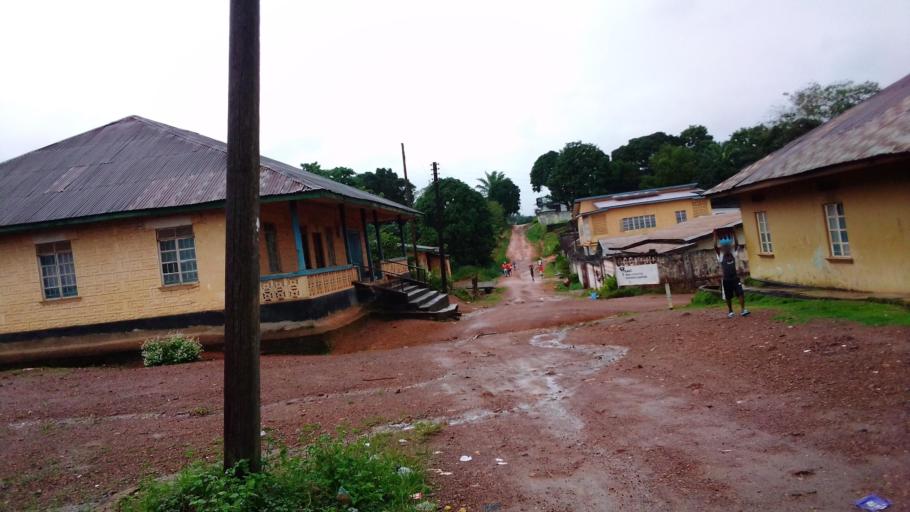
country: SL
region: Eastern Province
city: Kenema
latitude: 7.8903
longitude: -11.1904
